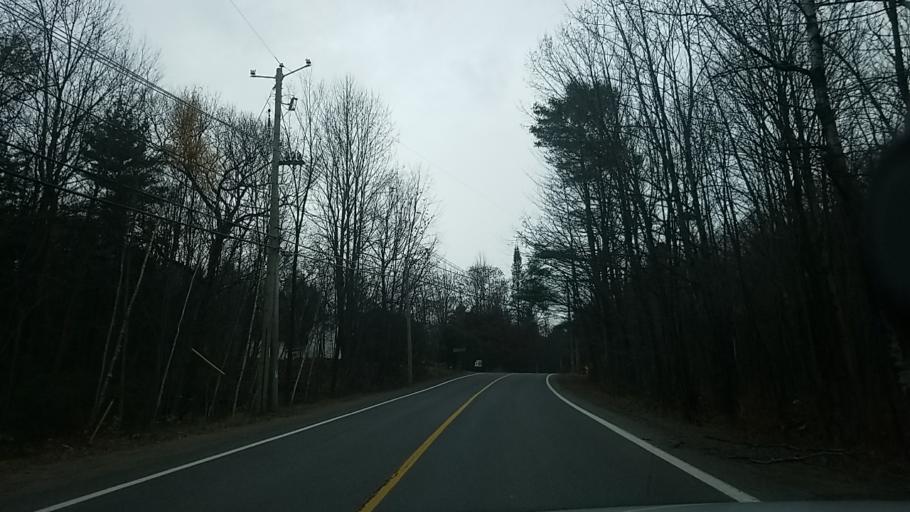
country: CA
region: Quebec
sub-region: Laurentides
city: Saint-Colomban
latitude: 45.7881
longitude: -74.1175
